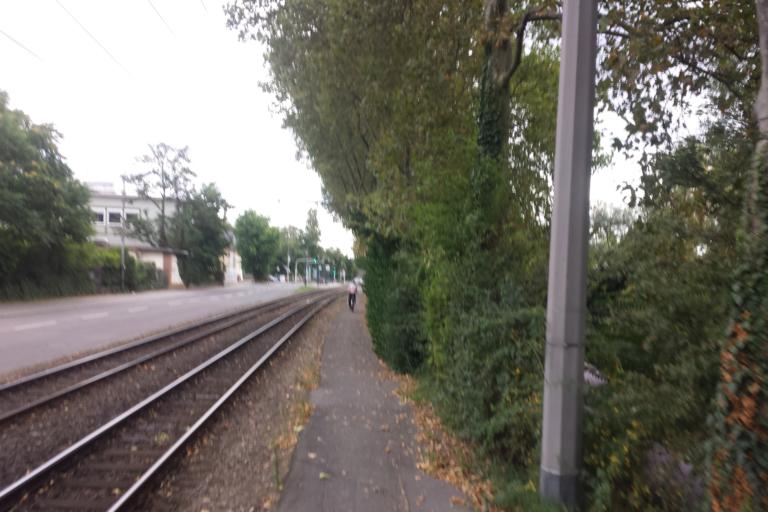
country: DE
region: Baden-Wuerttemberg
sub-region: Karlsruhe Region
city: Mannheim
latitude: 49.5267
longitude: 8.4704
